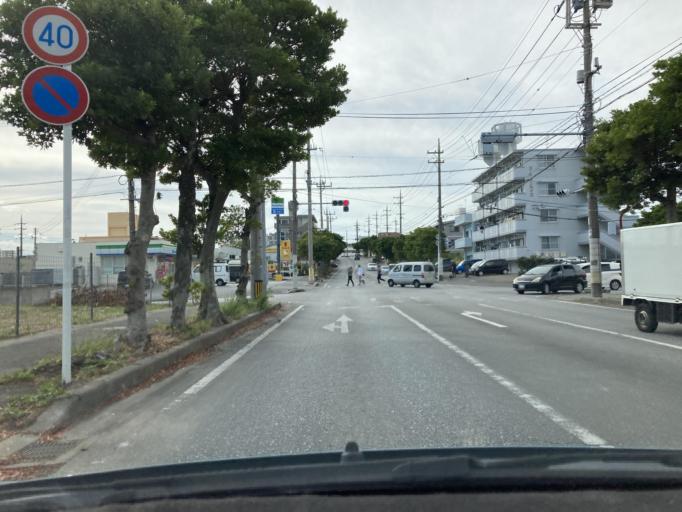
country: JP
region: Okinawa
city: Okinawa
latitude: 26.3459
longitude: 127.8312
